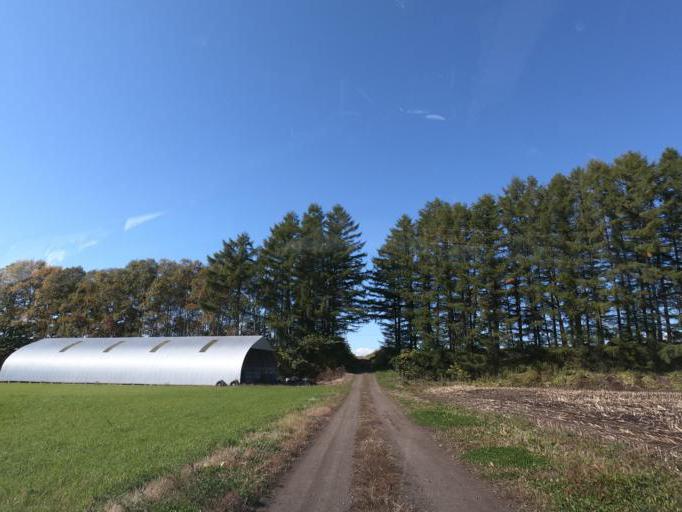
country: JP
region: Hokkaido
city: Otofuke
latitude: 43.0644
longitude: 143.2776
